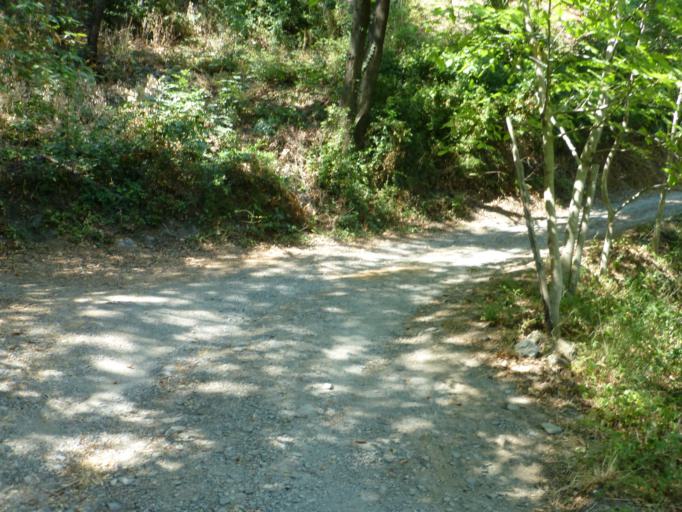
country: IT
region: Calabria
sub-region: Provincia di Reggio Calabria
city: Pazzano
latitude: 38.4802
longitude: 16.4457
